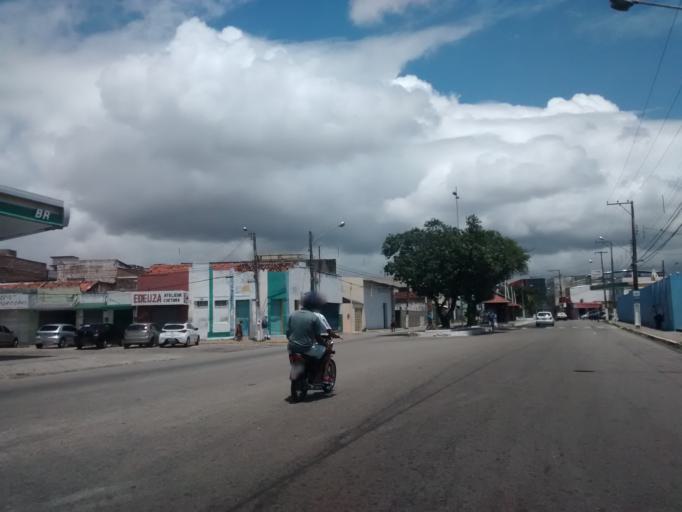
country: BR
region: Rio Grande do Norte
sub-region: Natal
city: Natal
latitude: -5.7929
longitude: -35.2134
